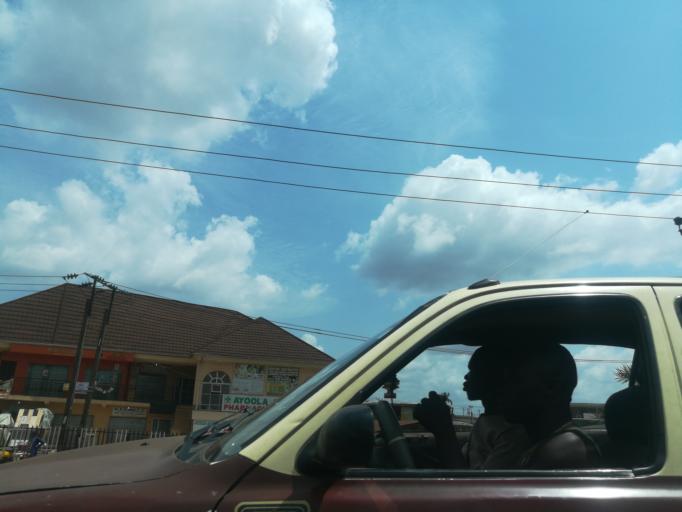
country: NG
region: Oyo
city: Ibadan
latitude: 7.4055
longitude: 3.9441
